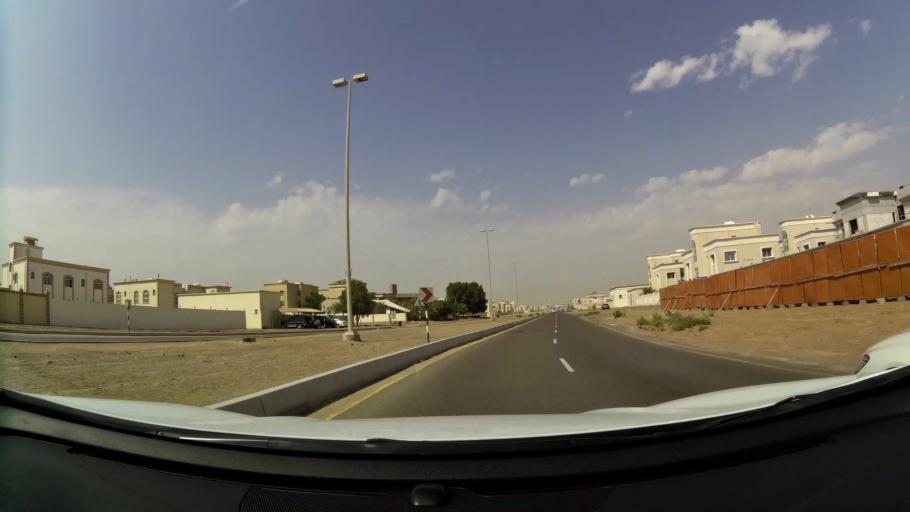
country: AE
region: Abu Dhabi
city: Abu Dhabi
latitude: 24.3332
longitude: 54.5489
